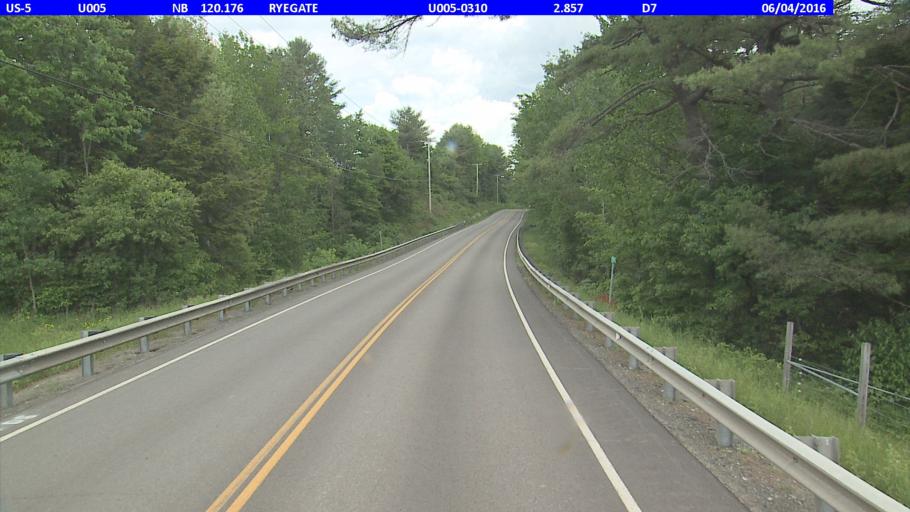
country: US
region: New Hampshire
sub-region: Grafton County
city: Woodsville
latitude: 44.1945
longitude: -72.0697
